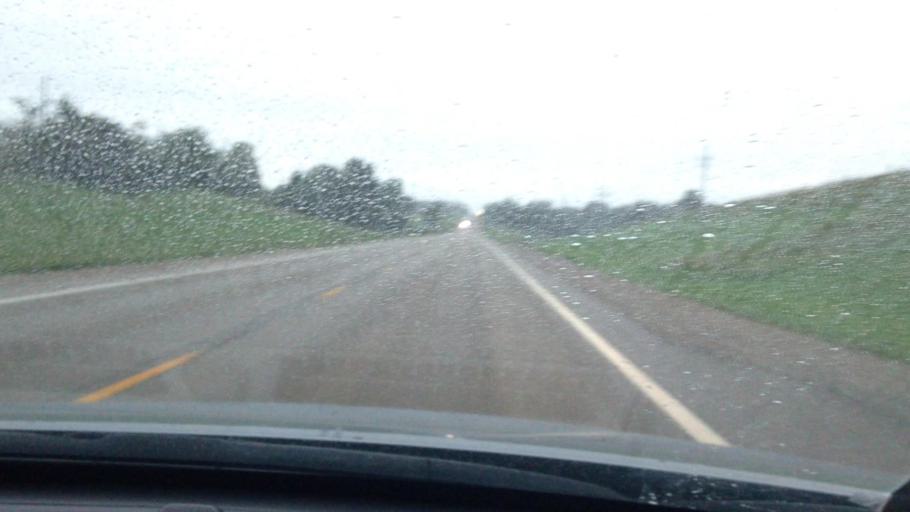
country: US
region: Kansas
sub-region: Brown County
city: Hiawatha
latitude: 39.8294
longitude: -95.5270
